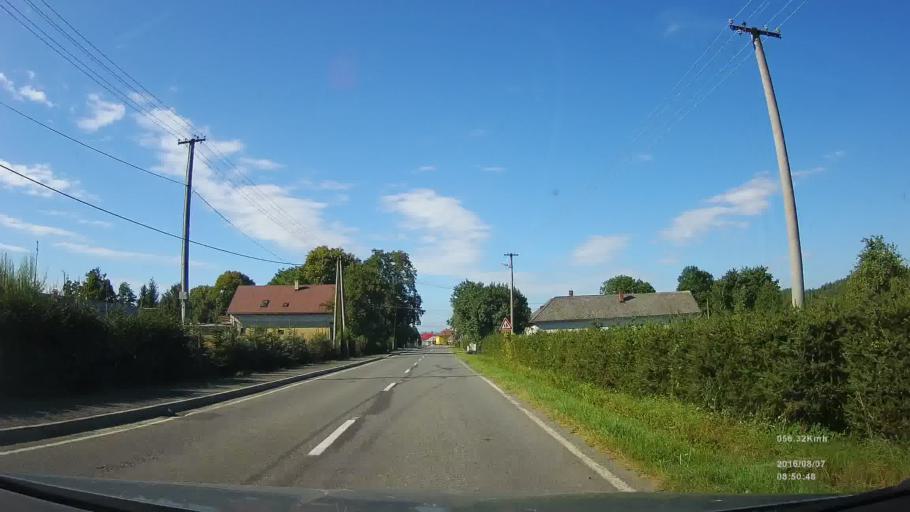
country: SK
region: Presovsky
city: Stropkov
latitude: 49.2433
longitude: 21.6796
